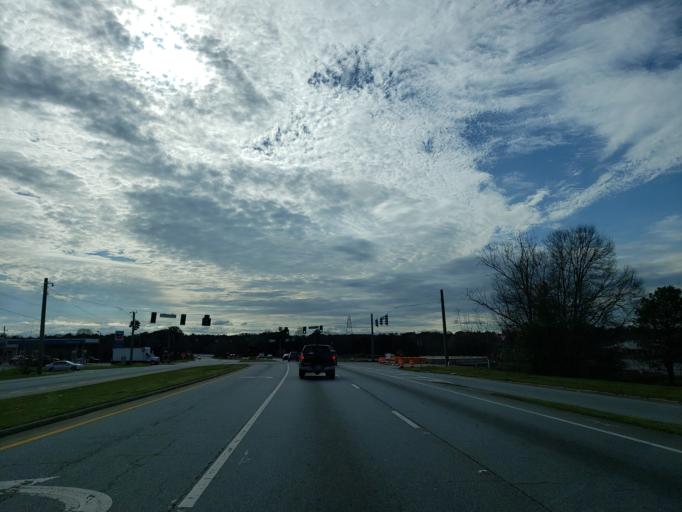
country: US
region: Georgia
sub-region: Clayton County
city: Forest Park
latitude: 33.6183
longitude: -84.3952
